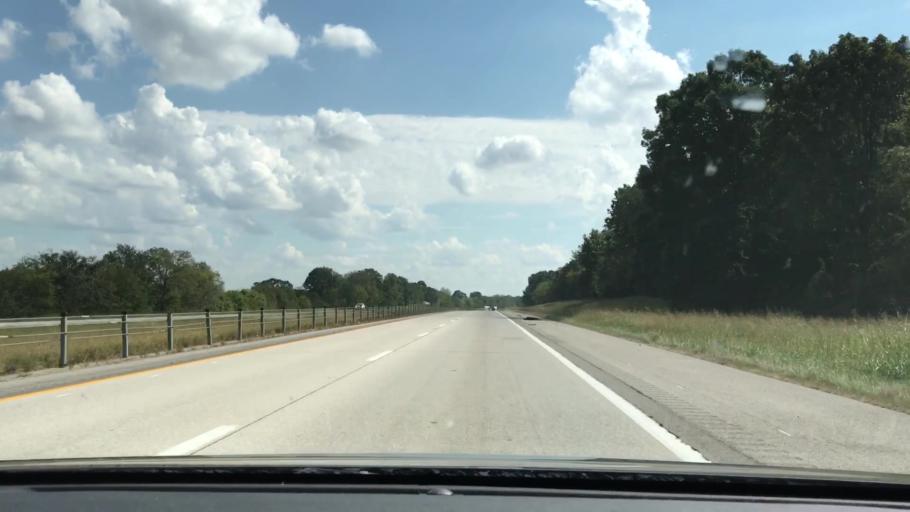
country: US
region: Kentucky
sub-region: Trigg County
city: Cadiz
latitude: 36.8478
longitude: -87.6857
